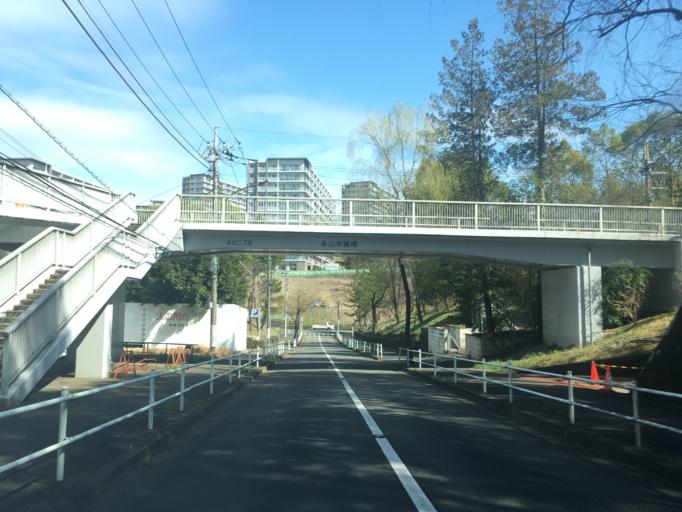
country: JP
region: Tokyo
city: Hino
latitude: 35.6247
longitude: 139.4484
